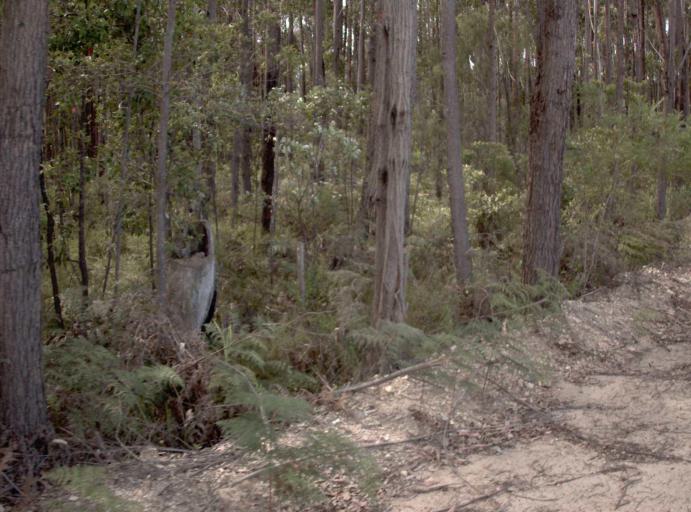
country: AU
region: Victoria
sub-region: East Gippsland
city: Lakes Entrance
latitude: -37.6237
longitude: 148.6783
